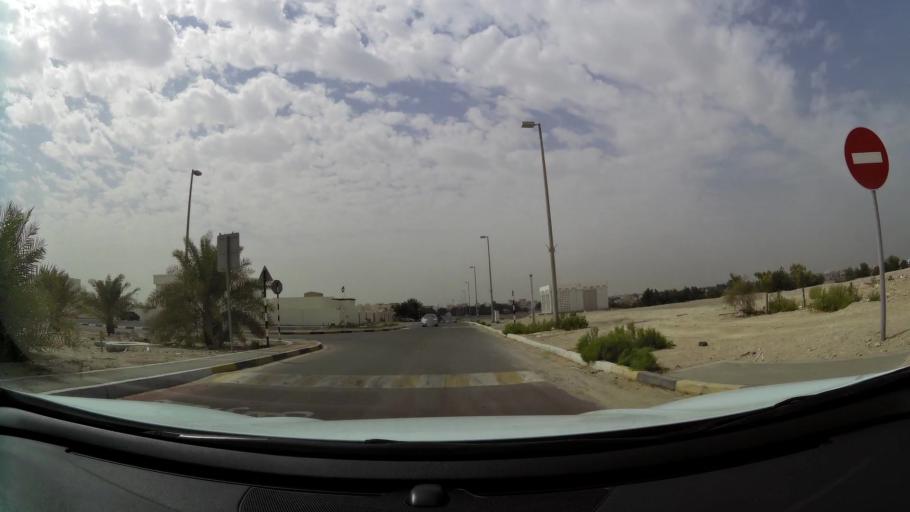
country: AE
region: Abu Dhabi
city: Abu Dhabi
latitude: 24.3054
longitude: 54.6359
